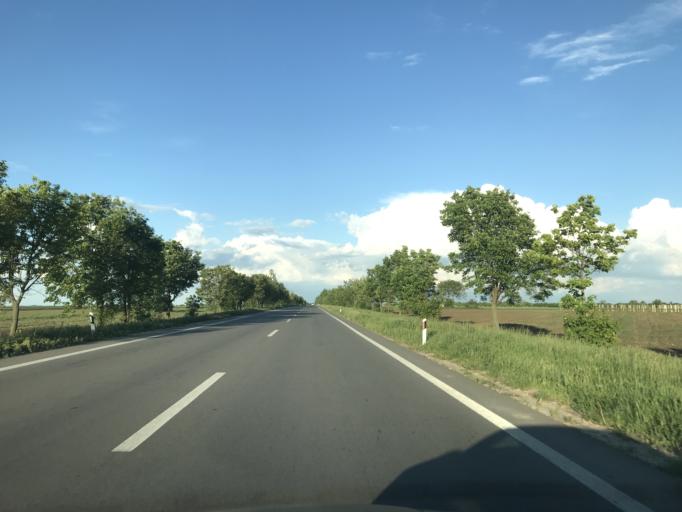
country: RS
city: Aradac
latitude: 45.3906
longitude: 20.2736
